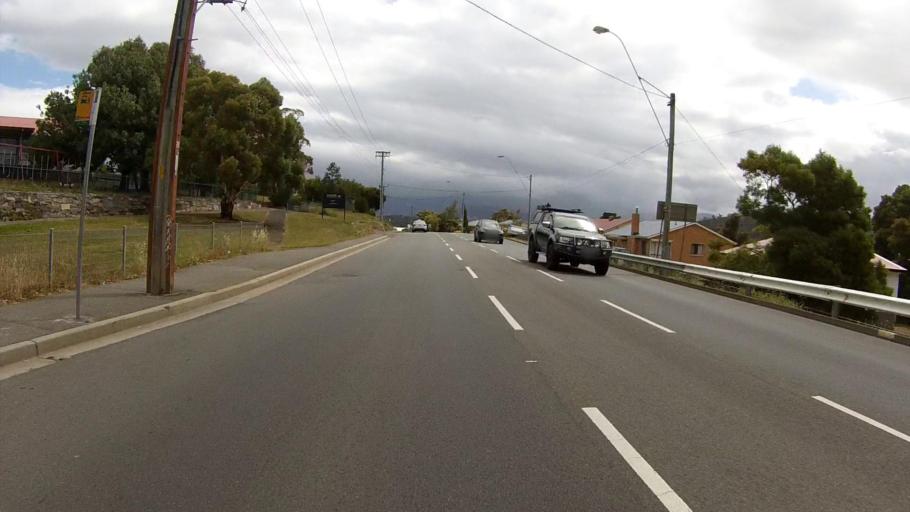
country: AU
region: Tasmania
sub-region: Clarence
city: Warrane
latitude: -42.8601
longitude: 147.3818
